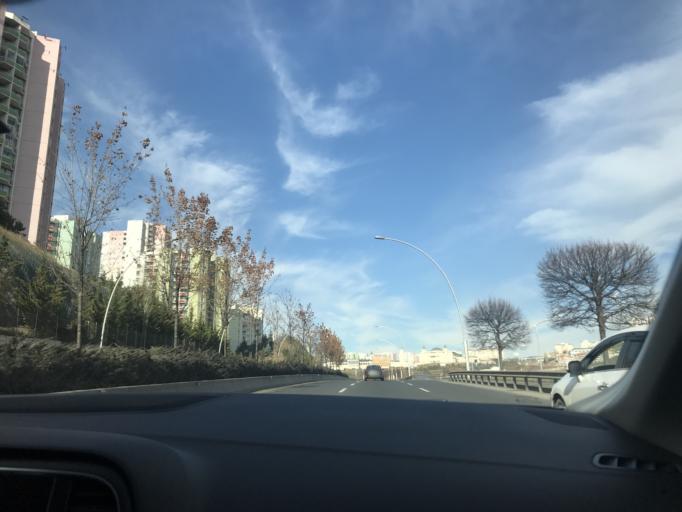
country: TR
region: Ankara
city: Mamak
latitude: 39.9986
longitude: 32.8948
